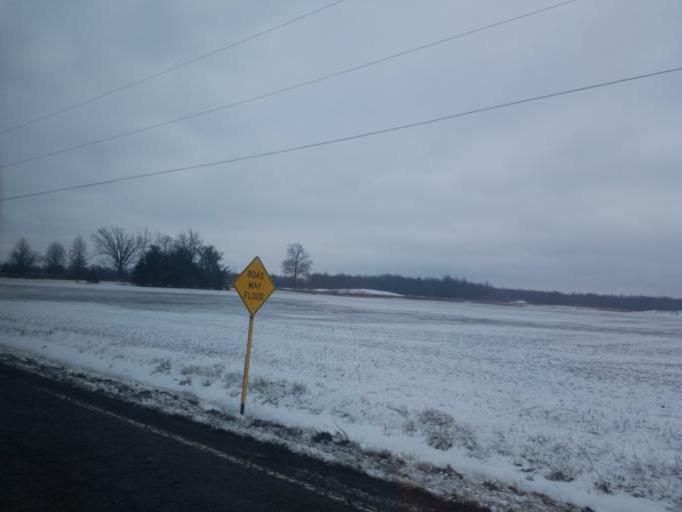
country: US
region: Ohio
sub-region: Licking County
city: Johnstown
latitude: 40.0963
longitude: -82.7339
